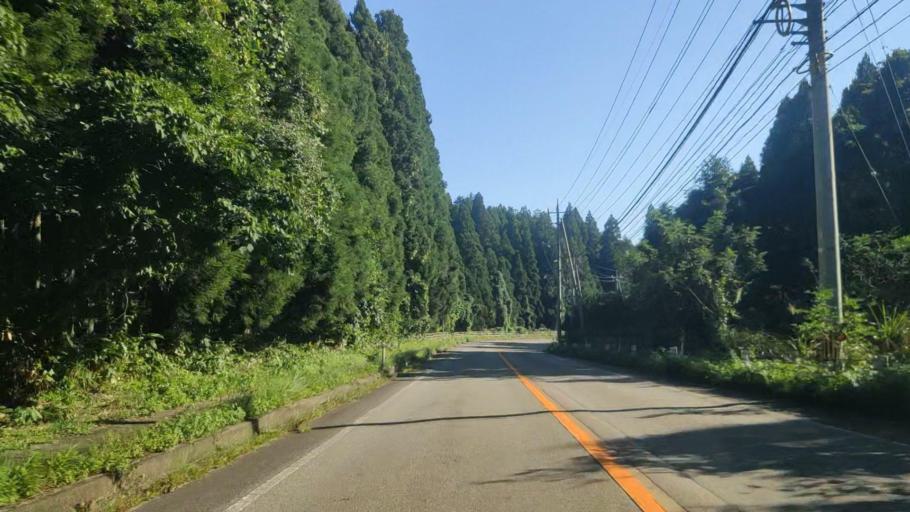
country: JP
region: Ishikawa
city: Nanao
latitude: 37.1221
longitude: 136.8623
